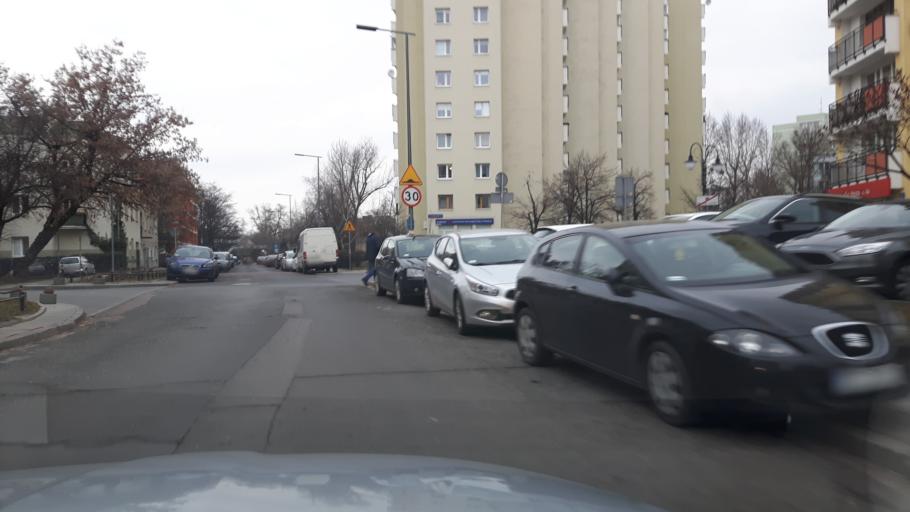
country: PL
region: Masovian Voivodeship
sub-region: Warszawa
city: Praga Poludnie
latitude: 52.2363
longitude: 21.0828
